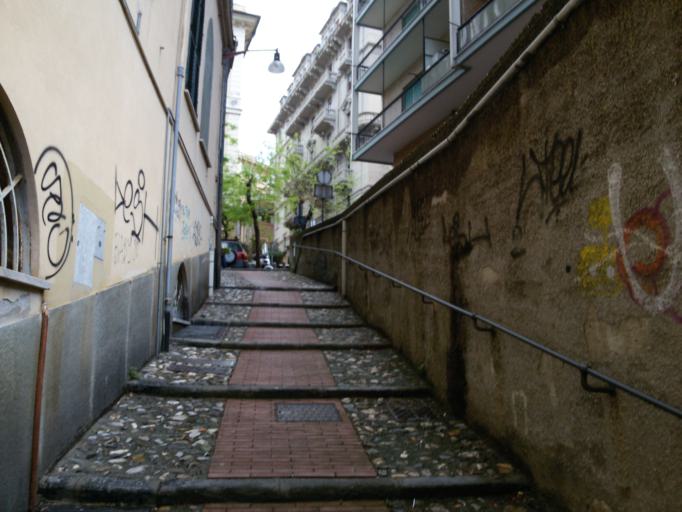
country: IT
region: Liguria
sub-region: Provincia di Genova
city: Genoa
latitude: 44.4146
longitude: 8.9318
